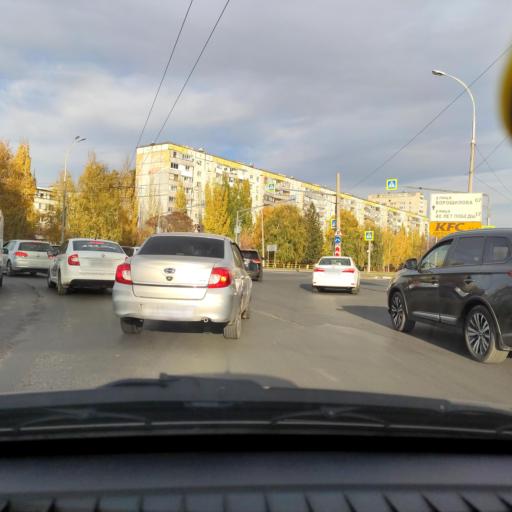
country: RU
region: Samara
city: Tol'yatti
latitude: 53.5272
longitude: 49.2976
